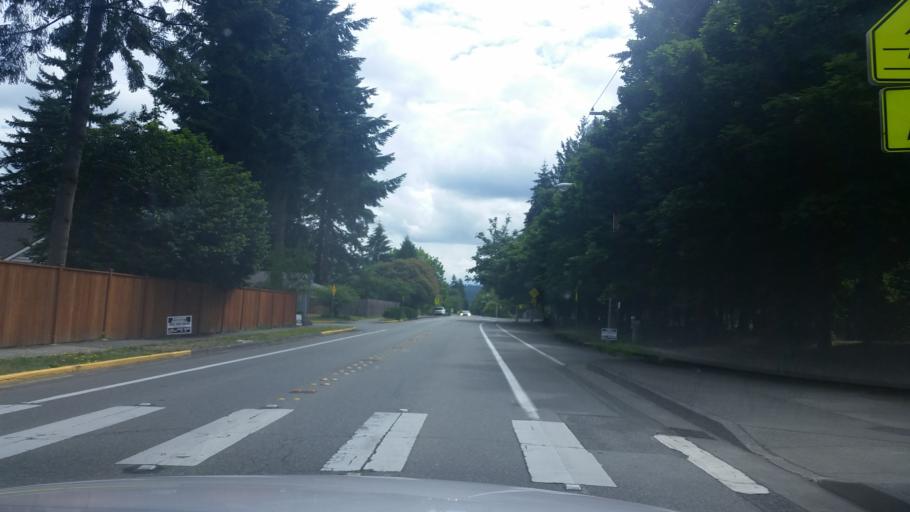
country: US
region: Washington
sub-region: King County
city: Redmond
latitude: 47.6929
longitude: -122.1124
